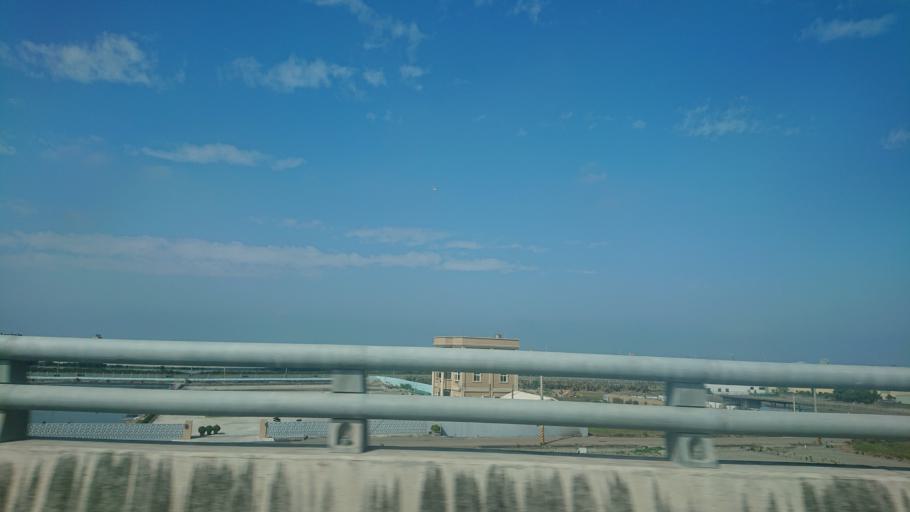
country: TW
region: Taiwan
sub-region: Changhua
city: Chang-hua
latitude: 24.0433
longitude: 120.4061
